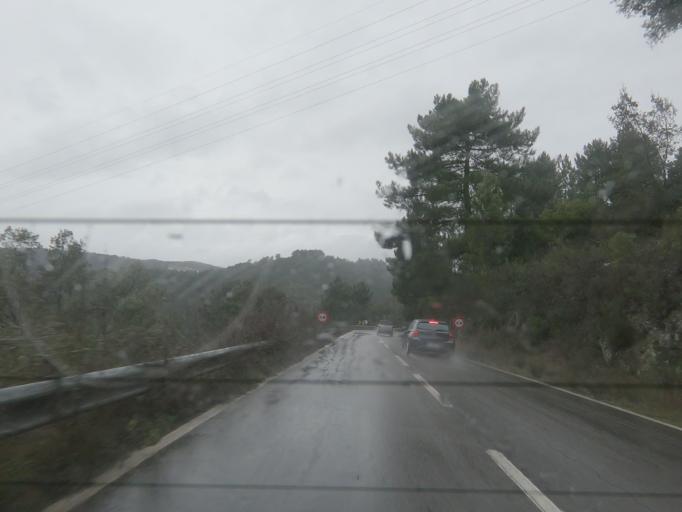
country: PT
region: Vila Real
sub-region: Vila Real
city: Vila Real
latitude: 41.2468
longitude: -7.6856
